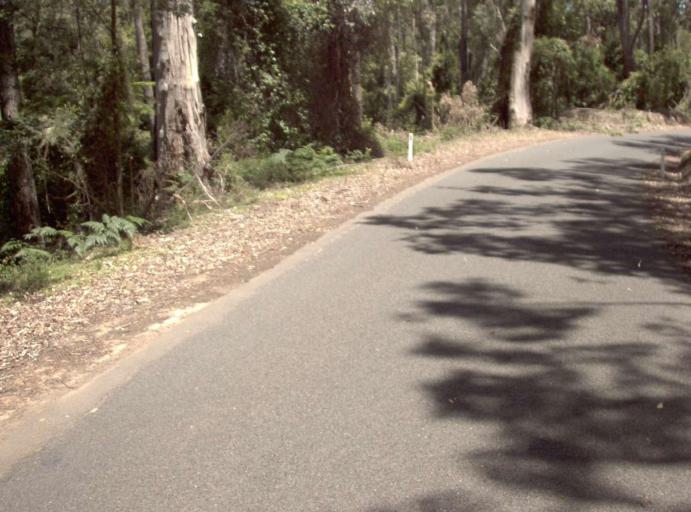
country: AU
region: New South Wales
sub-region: Bombala
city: Bombala
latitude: -37.4698
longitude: 148.9318
